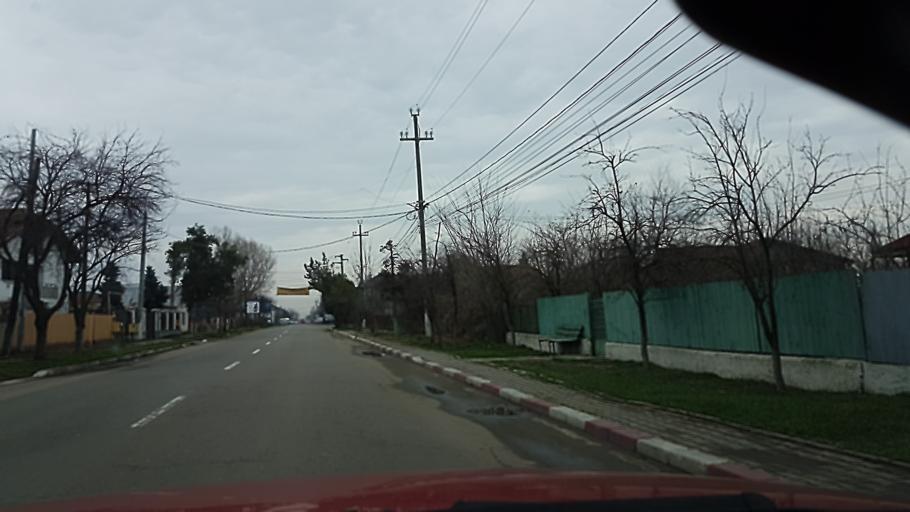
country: RO
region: Ilfov
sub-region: Comuna Corbeanca
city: Corbeanca
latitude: 44.6141
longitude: 26.0805
